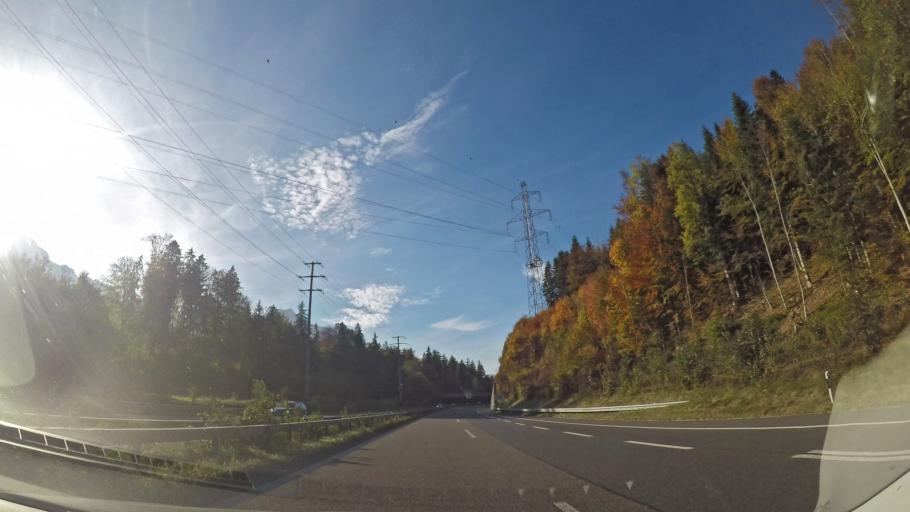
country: CH
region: Bern
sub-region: Frutigen-Niedersimmental District
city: Wimmis
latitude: 46.6947
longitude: 7.6466
